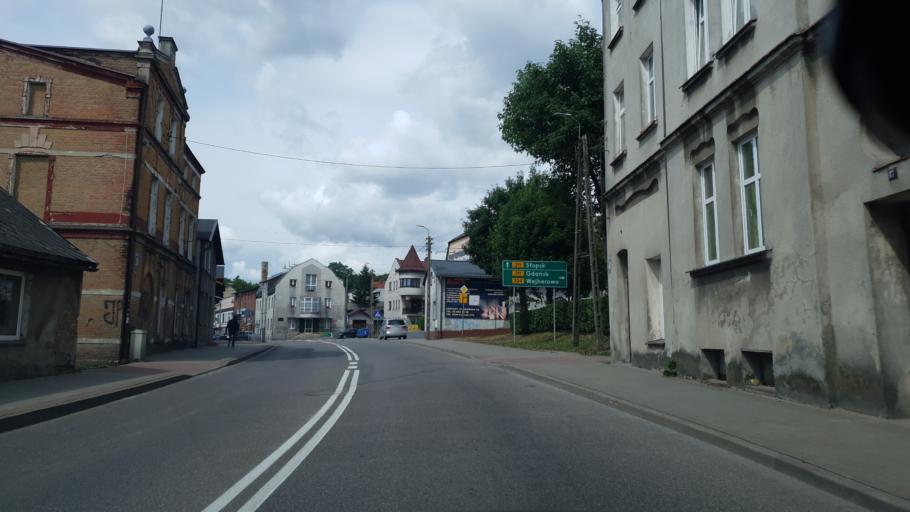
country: PL
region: Pomeranian Voivodeship
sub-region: Powiat kartuski
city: Kartuzy
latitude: 54.3309
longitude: 18.1983
